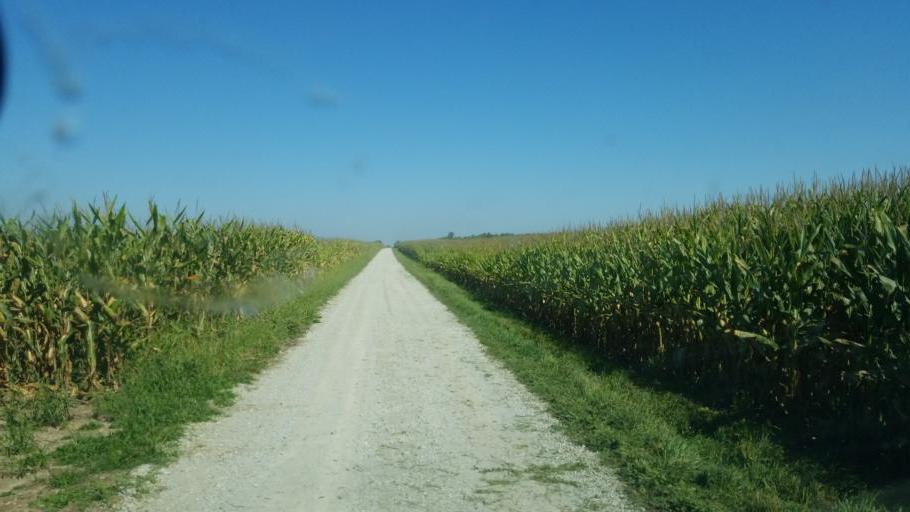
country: US
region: Ohio
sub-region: Hardin County
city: Kenton
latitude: 40.6381
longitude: -83.4962
